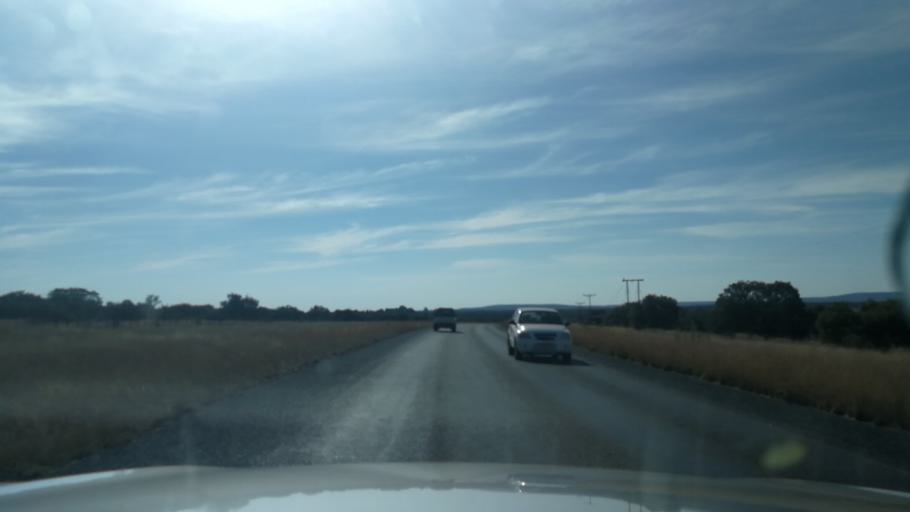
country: BW
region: South East
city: Janeng
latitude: -25.3270
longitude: 25.6172
